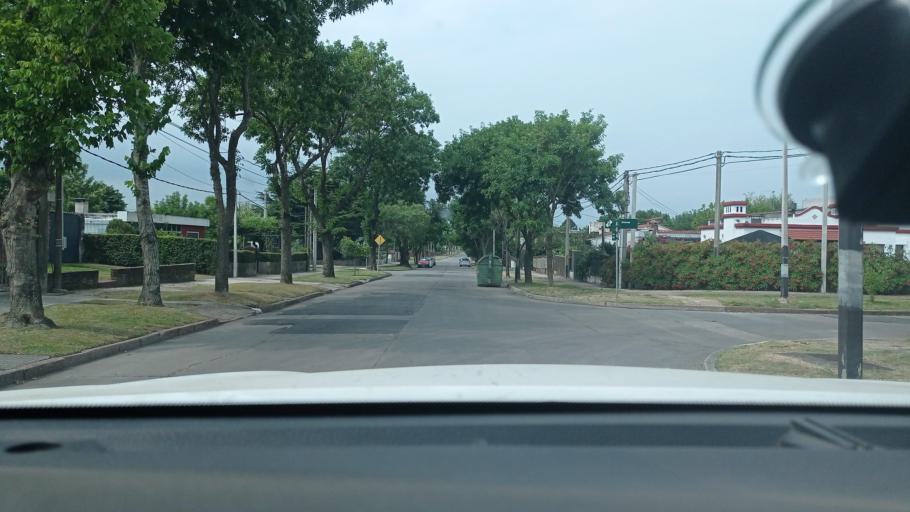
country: UY
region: Canelones
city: Paso de Carrasco
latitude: -34.8743
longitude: -56.0908
